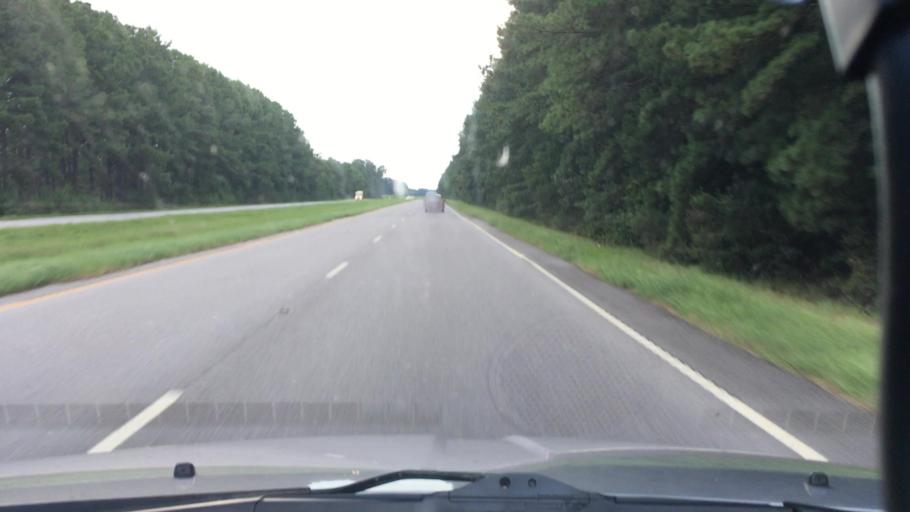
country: US
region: South Carolina
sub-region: Hampton County
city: Yemassee
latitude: 32.6212
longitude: -80.8227
